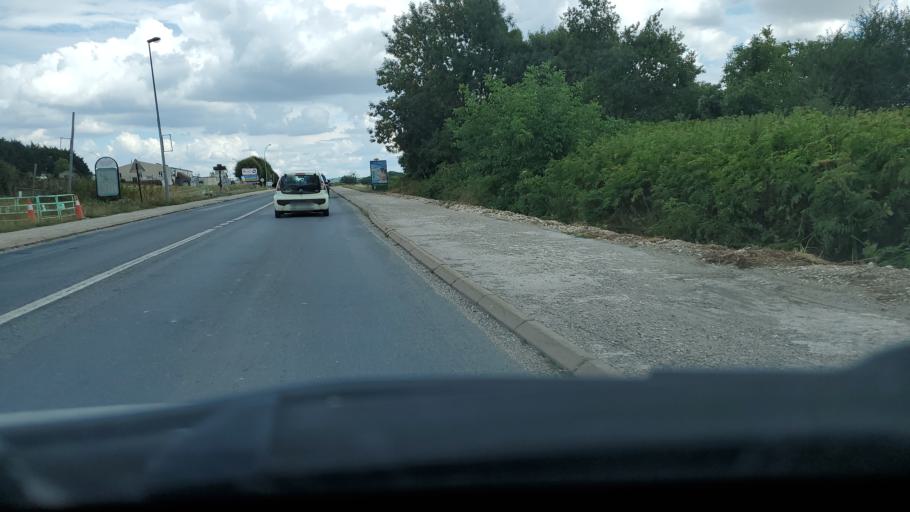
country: FR
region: Ile-de-France
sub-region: Departement de Seine-et-Marne
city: Mouroux
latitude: 48.8173
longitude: 3.0563
